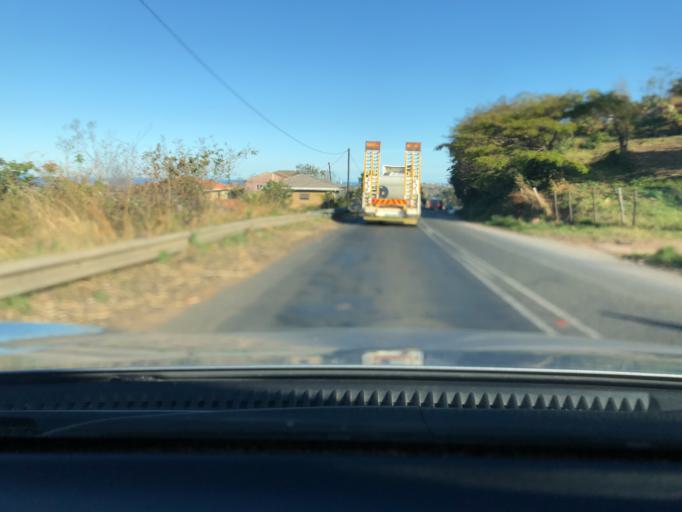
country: ZA
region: KwaZulu-Natal
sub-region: eThekwini Metropolitan Municipality
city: Umkomaas
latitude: -30.0228
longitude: 30.8114
